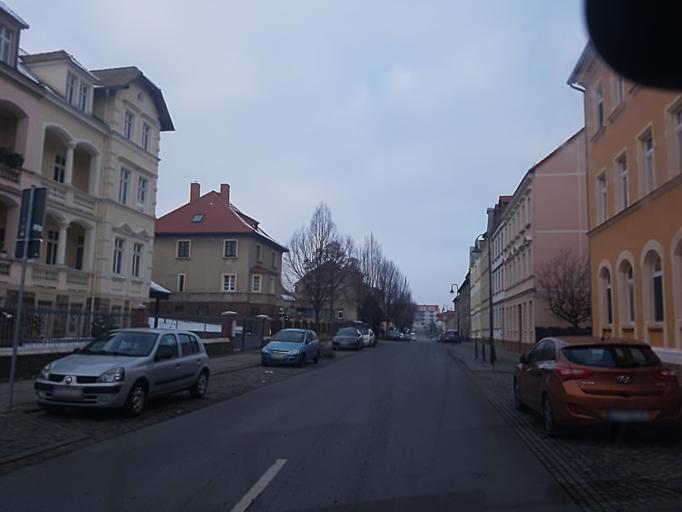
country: DE
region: Saxony
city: Oschatz
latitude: 51.2946
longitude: 13.1022
